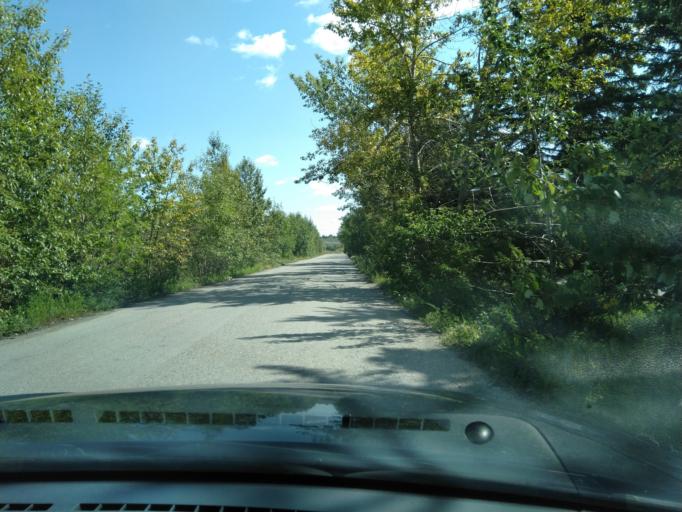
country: CA
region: Alberta
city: Calgary
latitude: 51.1015
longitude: -114.2157
